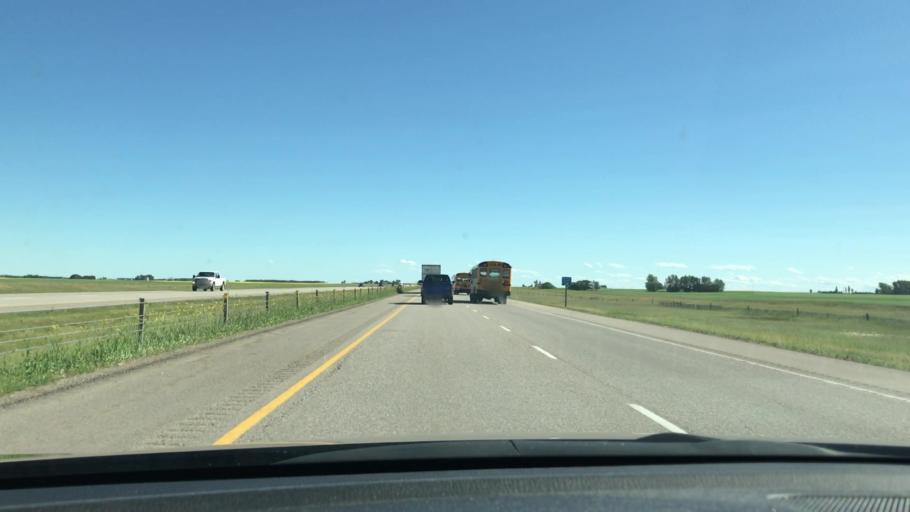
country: CA
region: Alberta
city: Didsbury
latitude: 51.6951
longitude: -114.0256
